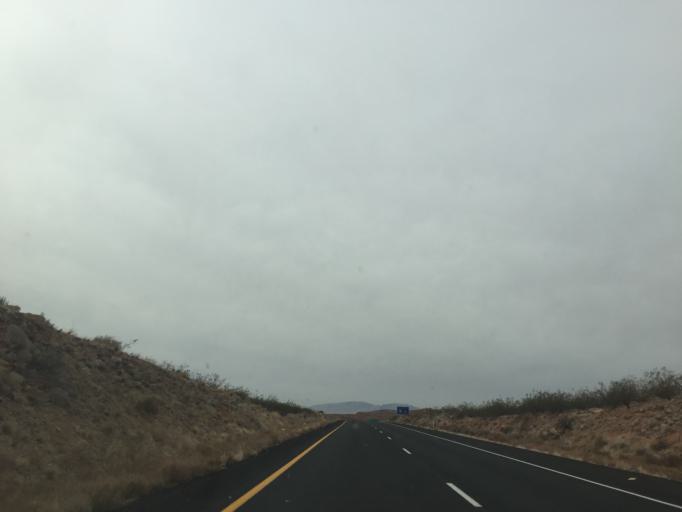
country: US
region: Utah
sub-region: Washington County
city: Washington
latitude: 37.1764
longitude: -113.4275
